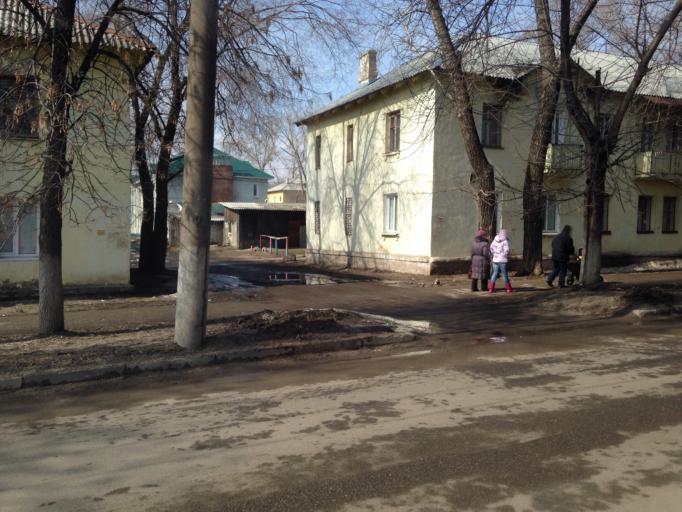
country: RU
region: Ulyanovsk
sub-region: Ulyanovskiy Rayon
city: Ulyanovsk
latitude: 54.3385
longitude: 48.5495
